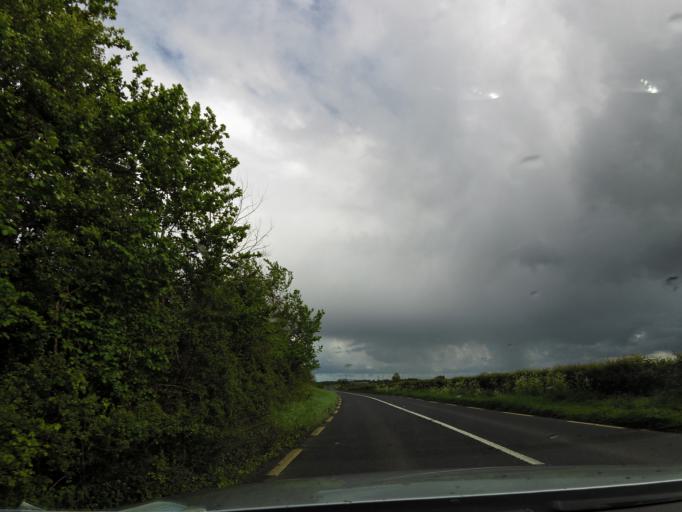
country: IE
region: Munster
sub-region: North Tipperary
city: Templemore
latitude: 52.7357
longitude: -7.8405
